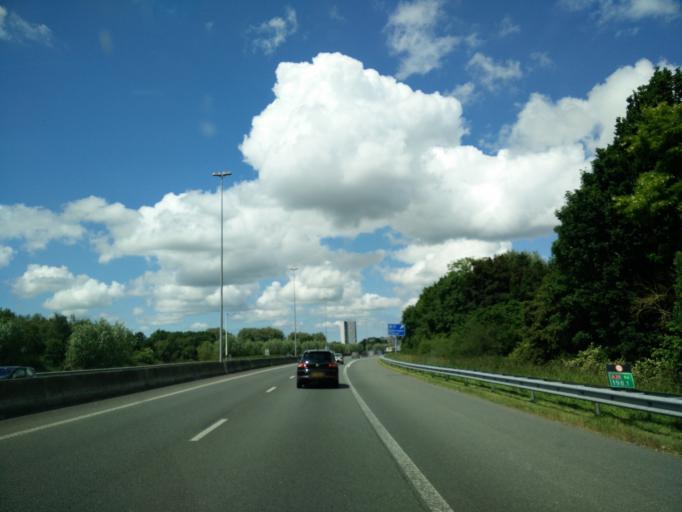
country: NL
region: Groningen
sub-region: Gemeente Groningen
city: Groningen
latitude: 53.1857
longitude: 6.5702
